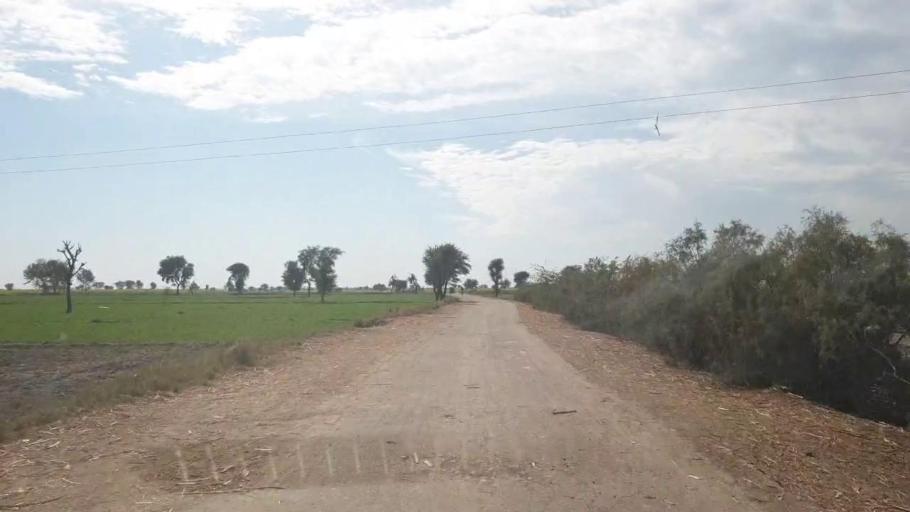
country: PK
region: Sindh
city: Sanghar
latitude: 26.0382
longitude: 68.9145
